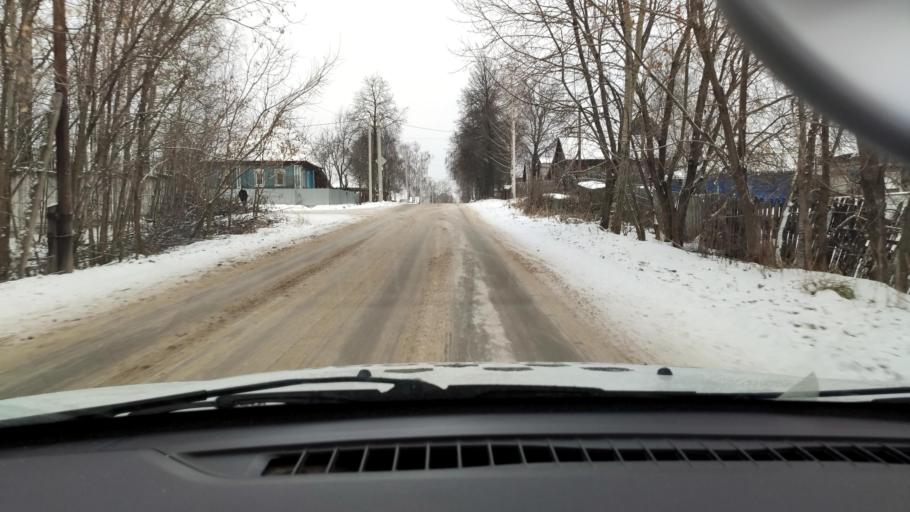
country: RU
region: Perm
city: Polazna
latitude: 58.1210
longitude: 56.3953
